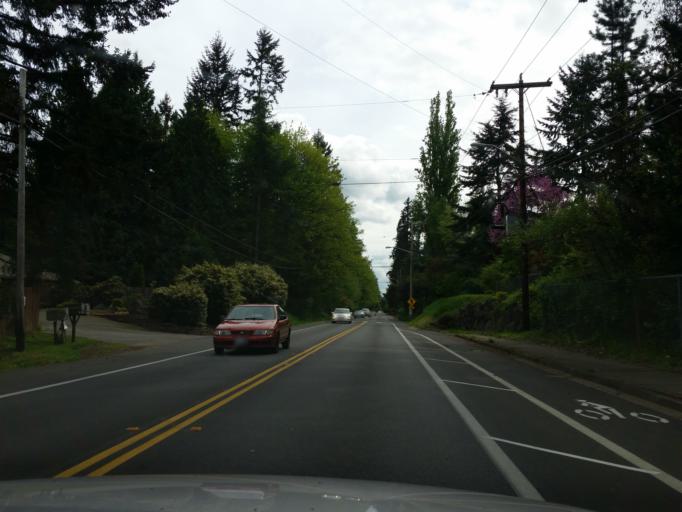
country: US
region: Washington
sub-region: King County
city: Kingsgate
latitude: 47.7030
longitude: -122.1646
